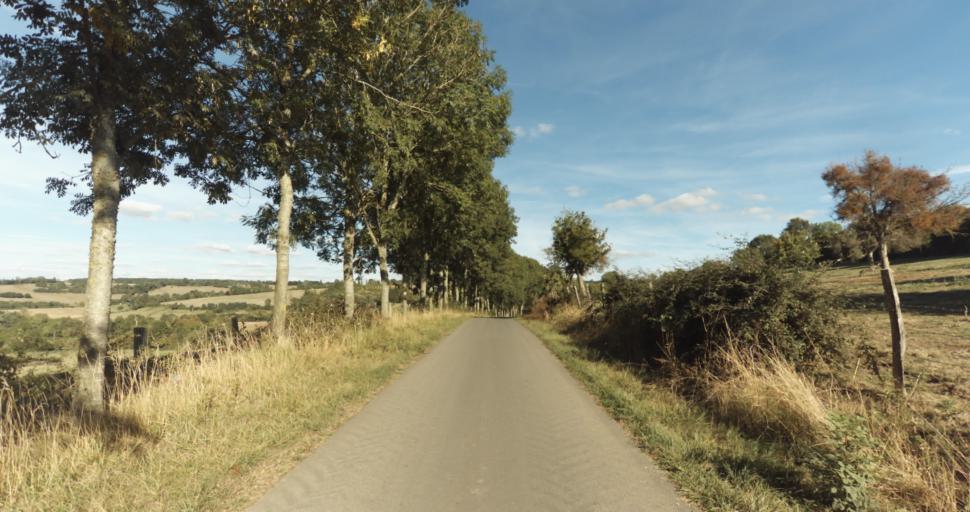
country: FR
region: Lower Normandy
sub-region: Departement de l'Orne
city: Vimoutiers
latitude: 48.9105
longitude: 0.1235
